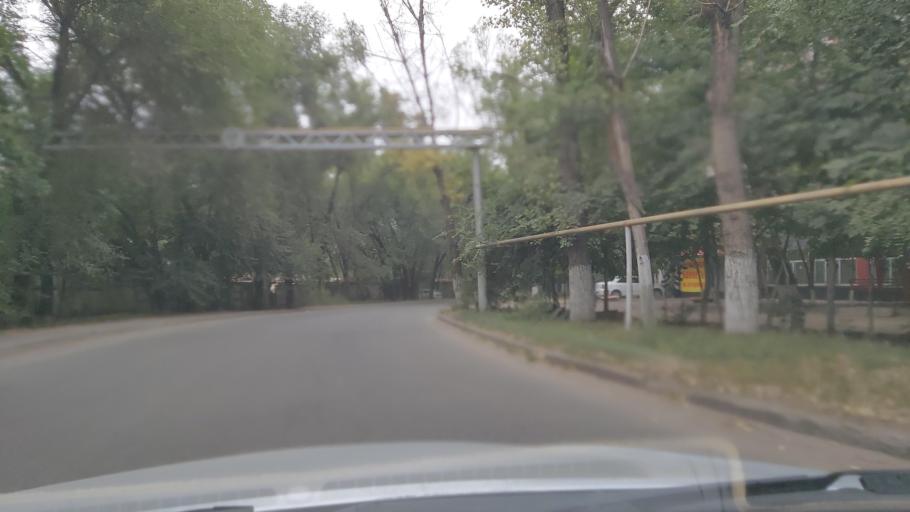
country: KZ
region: Almaty Oblysy
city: Pervomayskiy
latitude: 43.3513
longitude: 76.9749
